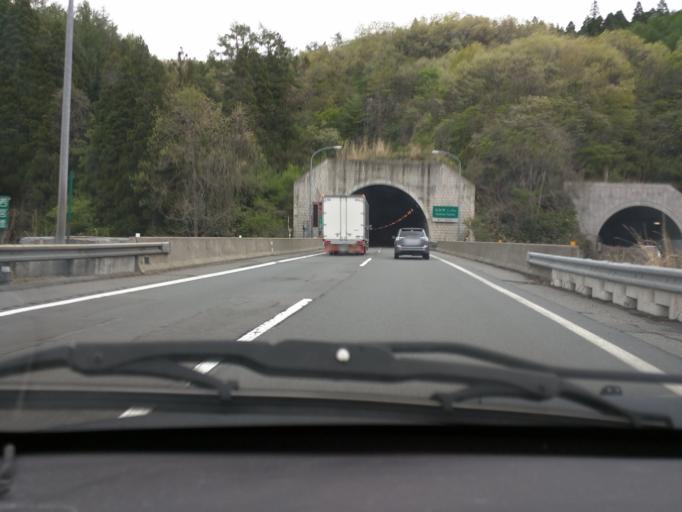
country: JP
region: Nagano
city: Nakano
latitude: 36.7948
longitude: 138.2614
